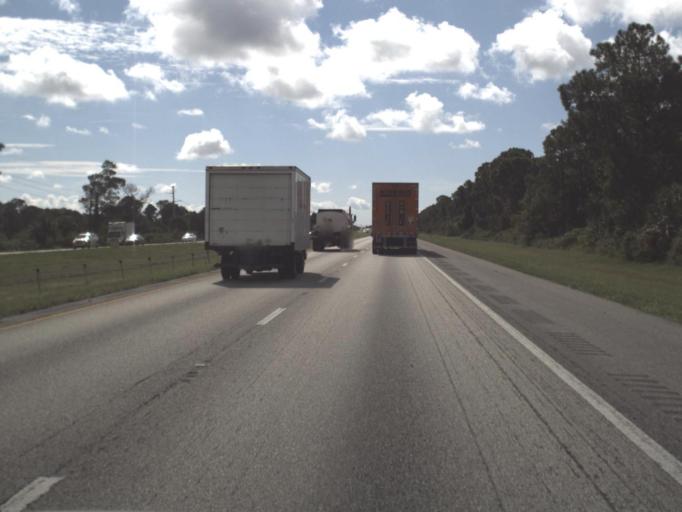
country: US
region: Florida
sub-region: Charlotte County
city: Port Charlotte
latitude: 27.0701
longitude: -82.0966
